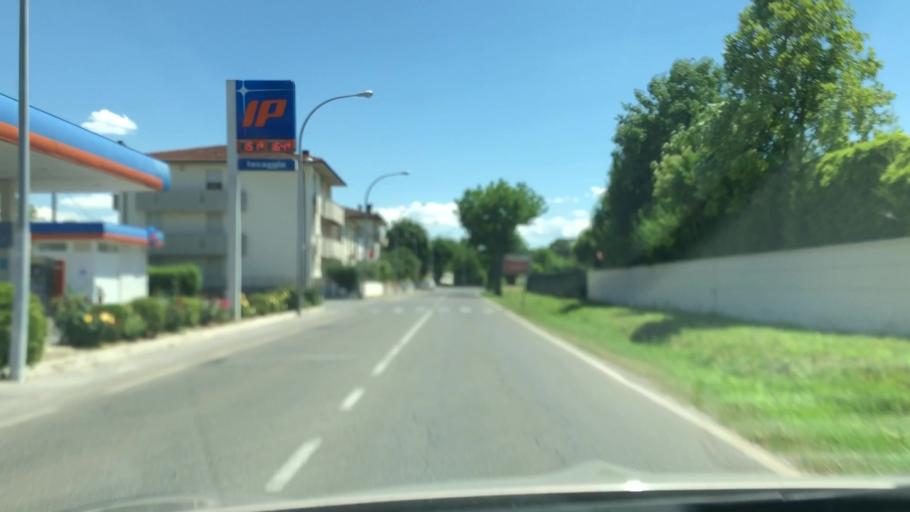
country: IT
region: Tuscany
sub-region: Province of Pisa
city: Ponsacco
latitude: 43.6152
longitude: 10.6409
